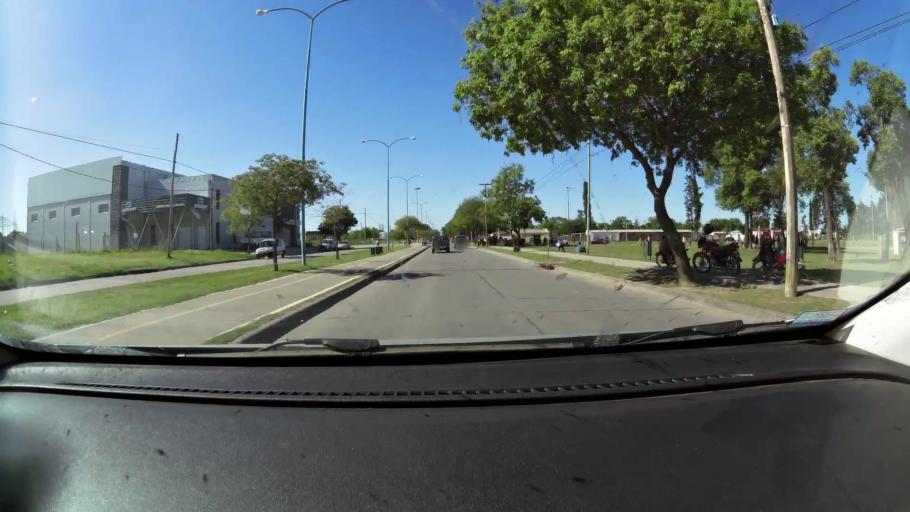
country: AR
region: Santa Fe
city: Rafaela
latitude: -31.2374
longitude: -61.4881
